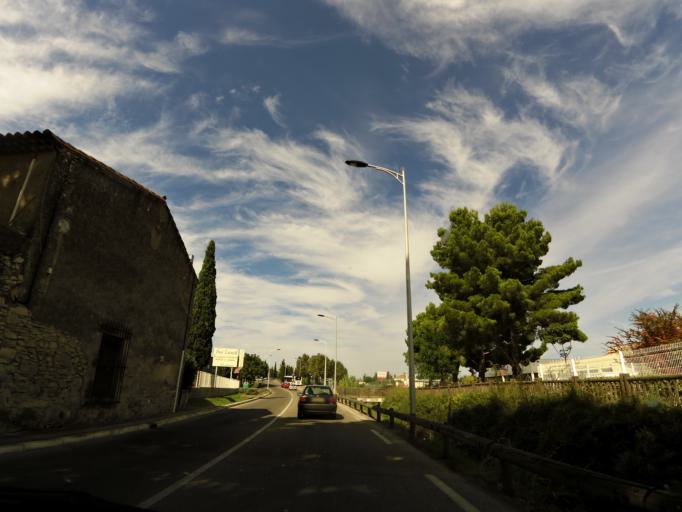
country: FR
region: Languedoc-Roussillon
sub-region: Departement du Gard
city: Caissargues
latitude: 43.8138
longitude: 4.3699
